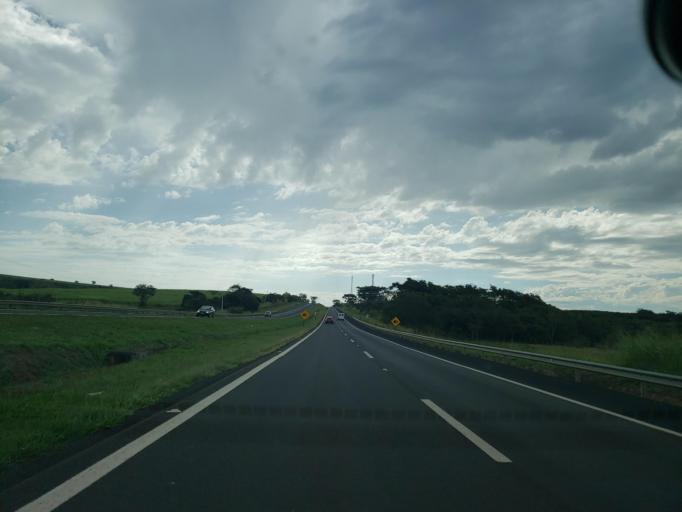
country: BR
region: Sao Paulo
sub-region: Cafelandia
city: Cafelandia
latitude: -21.7673
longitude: -49.6693
